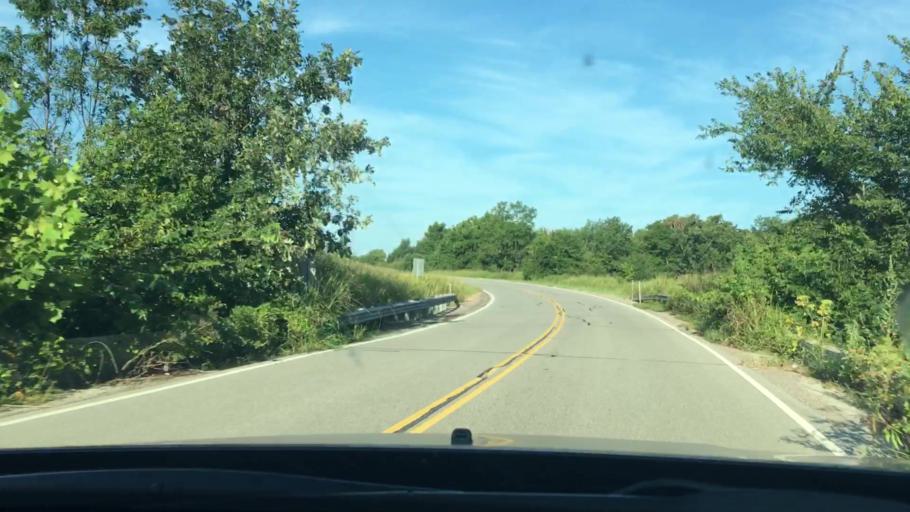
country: US
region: Oklahoma
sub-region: Pontotoc County
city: Ada
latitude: 34.6995
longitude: -96.4376
